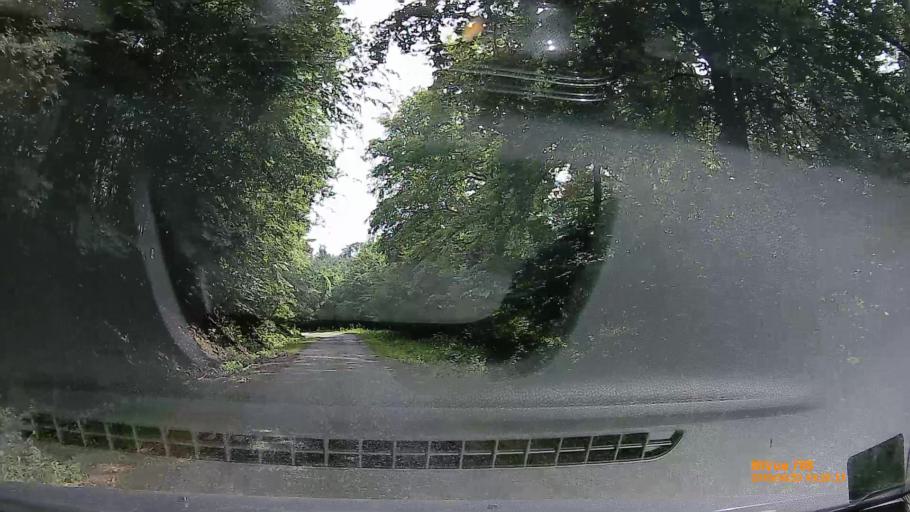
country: HU
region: Baranya
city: Mecseknadasd
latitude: 46.2060
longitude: 18.4934
